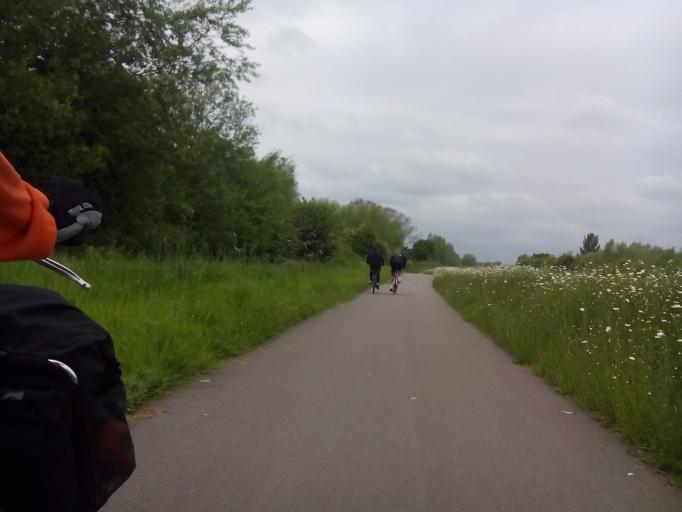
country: GB
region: England
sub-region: Cambridgeshire
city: Needingworth
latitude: 52.3091
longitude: -0.0429
